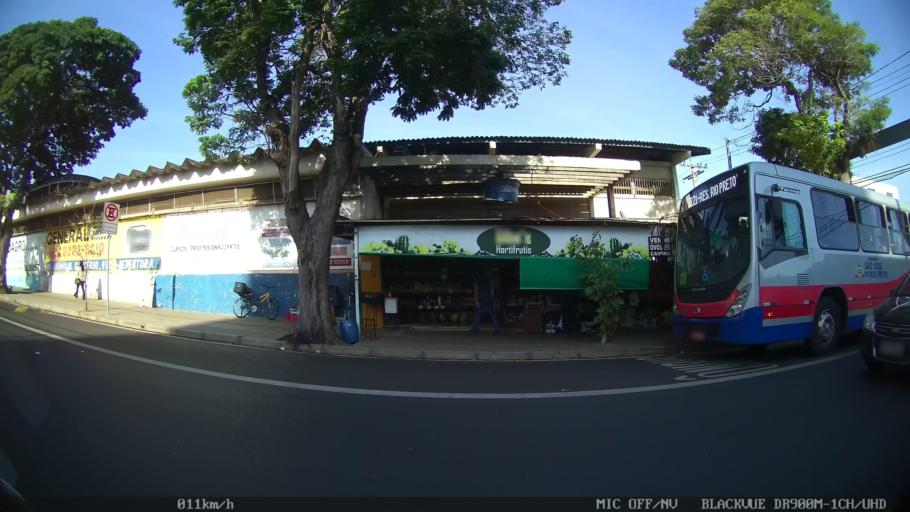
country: BR
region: Sao Paulo
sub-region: Sao Jose Do Rio Preto
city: Sao Jose do Rio Preto
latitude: -20.8030
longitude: -49.3718
